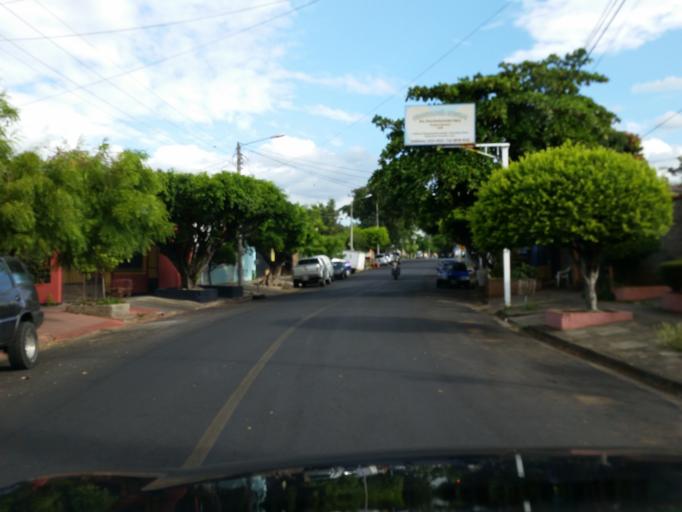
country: NI
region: Managua
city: Managua
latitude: 12.1267
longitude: -86.2582
